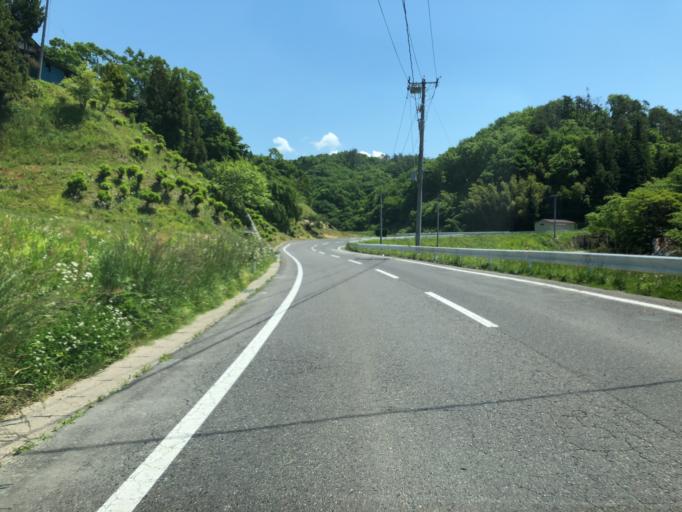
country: JP
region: Fukushima
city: Miharu
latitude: 37.4965
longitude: 140.5058
